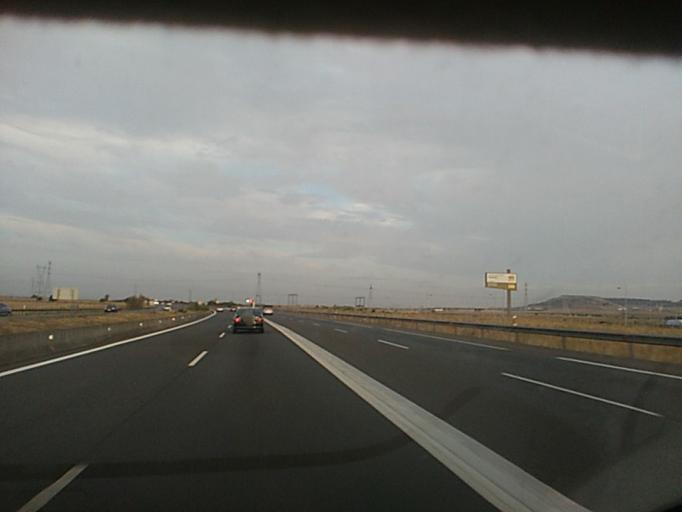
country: ES
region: Castille and Leon
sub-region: Provincia de Valladolid
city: Tordesillas
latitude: 41.5136
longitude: -5.0048
